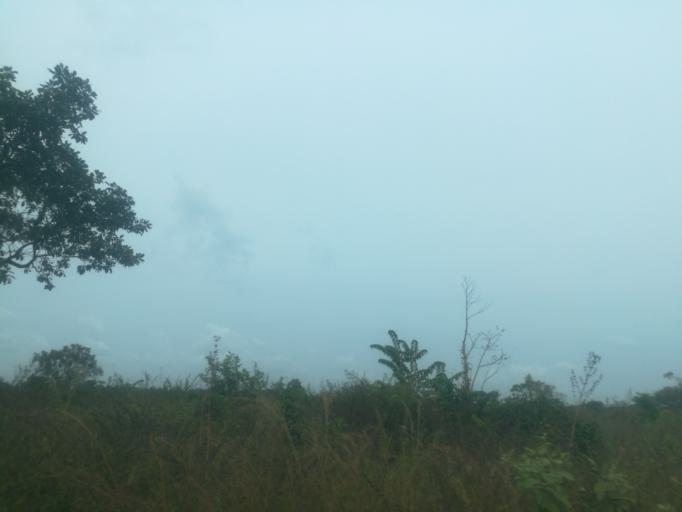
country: NG
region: Ogun
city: Ayetoro
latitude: 7.2708
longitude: 3.1030
